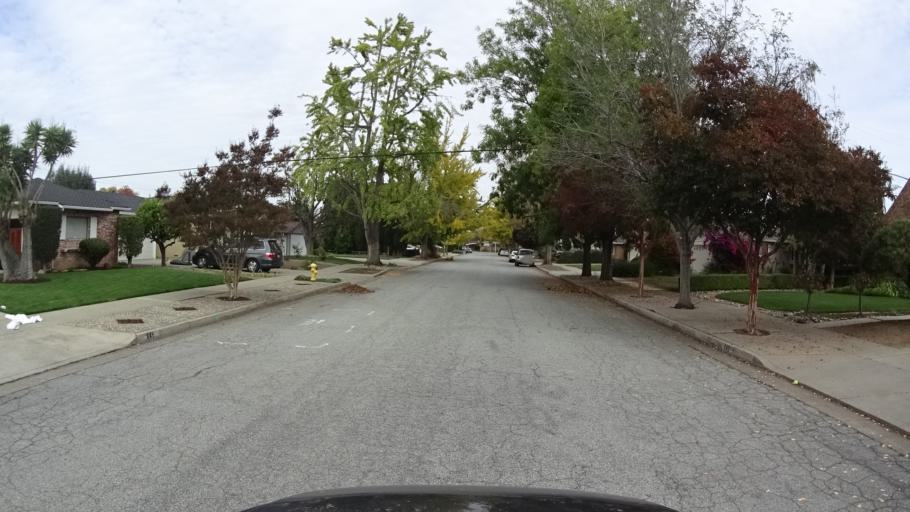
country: US
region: California
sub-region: Santa Clara County
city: Burbank
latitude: 37.3282
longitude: -121.9555
